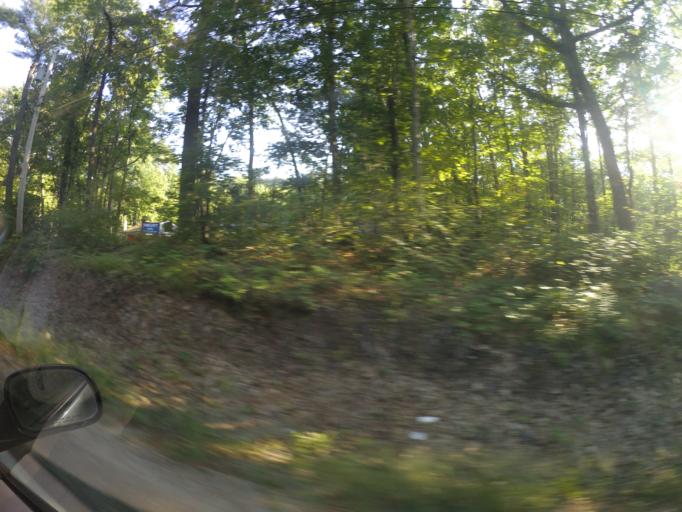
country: US
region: Maine
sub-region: Cumberland County
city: Raymond
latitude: 43.8966
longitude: -70.4508
